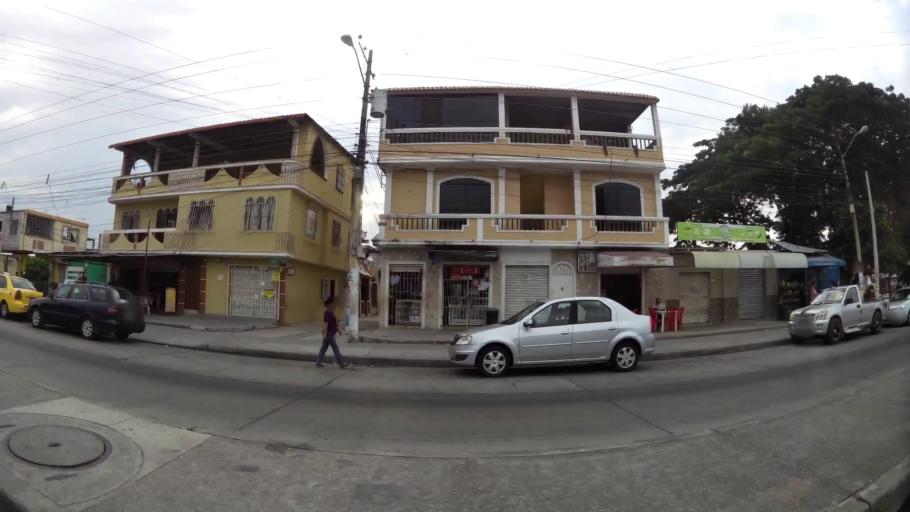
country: EC
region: Guayas
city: Guayaquil
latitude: -2.2528
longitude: -79.8820
